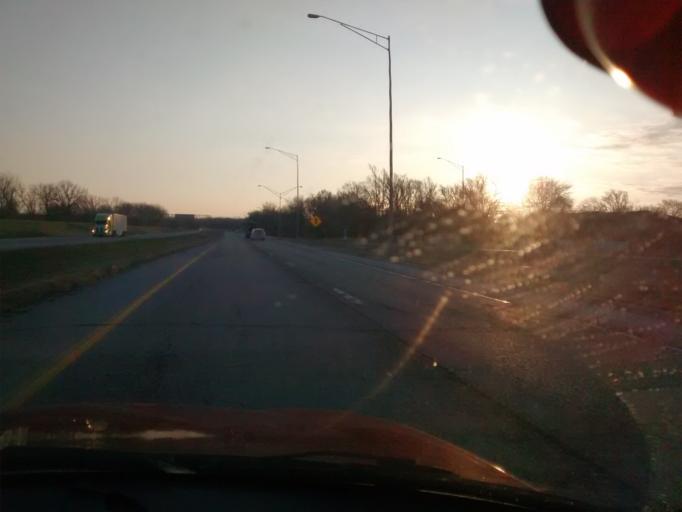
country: US
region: Iowa
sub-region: Pottawattamie County
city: Carter Lake
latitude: 41.2714
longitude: -95.9018
